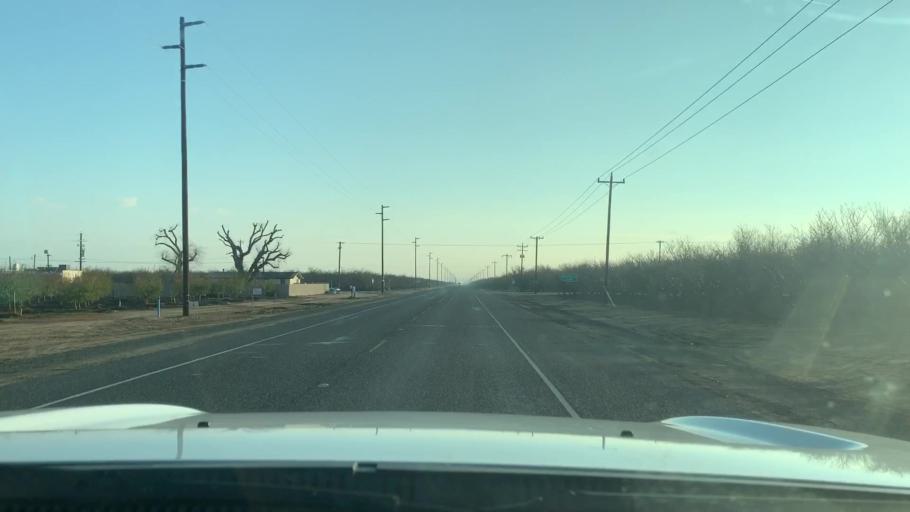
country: US
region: California
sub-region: Kern County
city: Wasco
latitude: 35.6011
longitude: -119.4751
